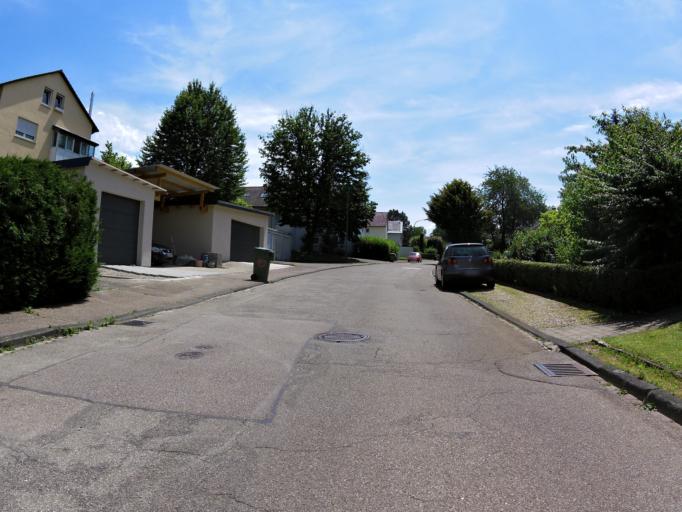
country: DE
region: Baden-Wuerttemberg
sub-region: Freiburg Region
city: Lahr
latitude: 48.3298
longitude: 7.8649
